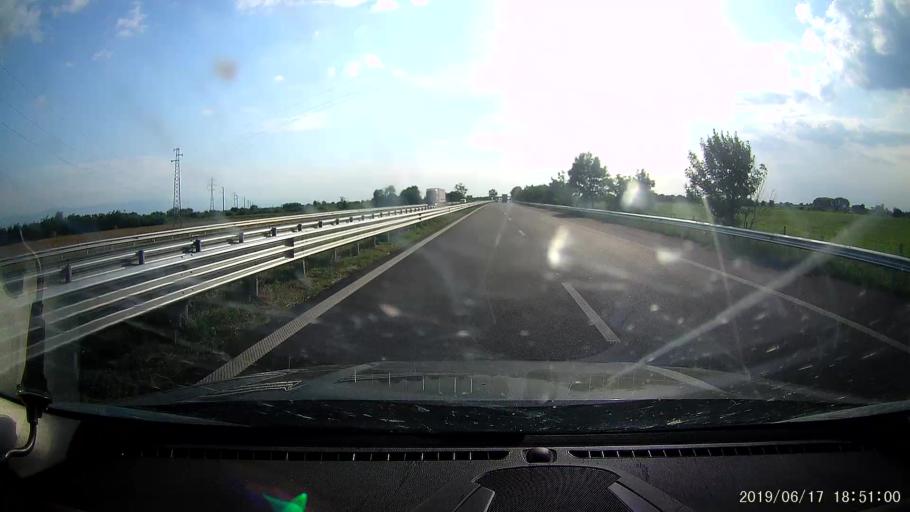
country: BG
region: Plovdiv
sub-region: Obshtina Rakovski
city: Rakovski
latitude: 42.2136
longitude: 24.9847
